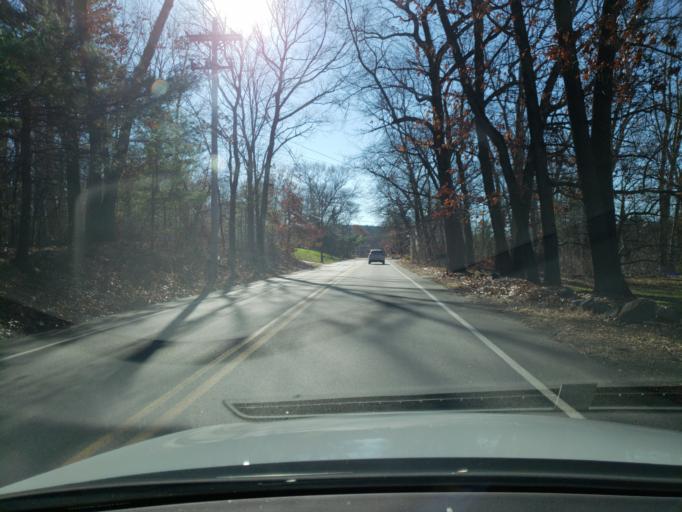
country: US
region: Massachusetts
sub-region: Essex County
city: Andover
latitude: 42.6766
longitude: -71.1345
